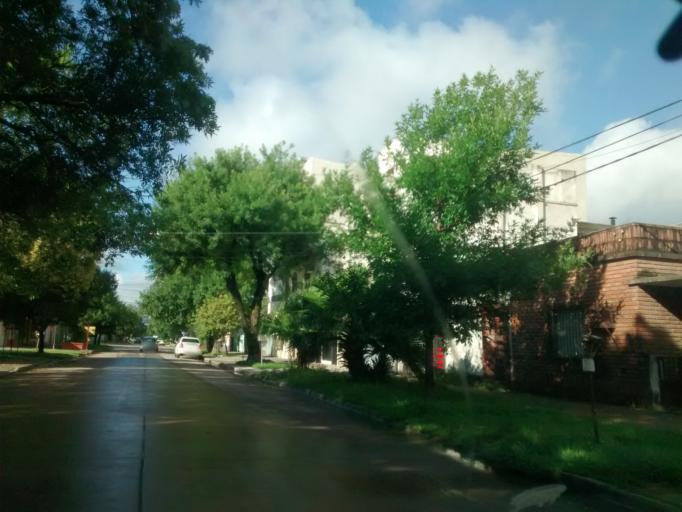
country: AR
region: Chaco
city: Resistencia
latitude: -27.4598
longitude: -58.9893
